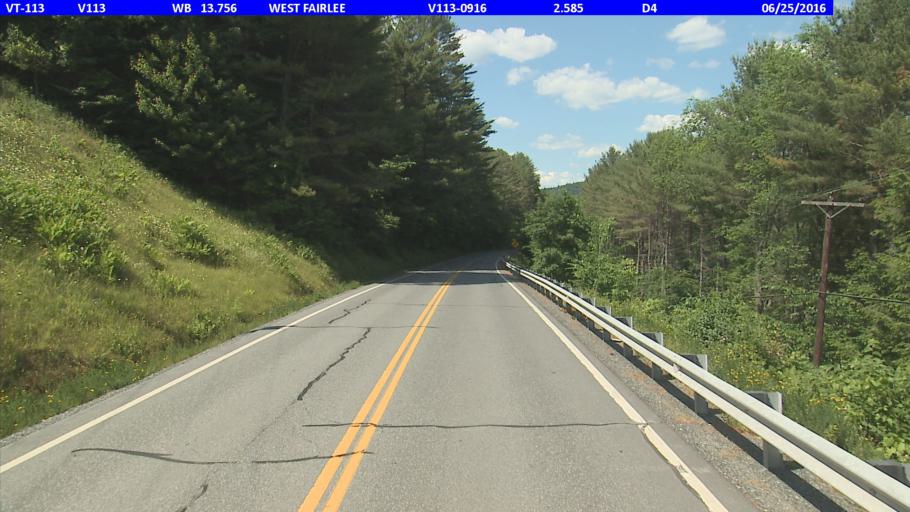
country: US
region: New Hampshire
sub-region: Grafton County
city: Orford
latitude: 43.9005
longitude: -72.2634
